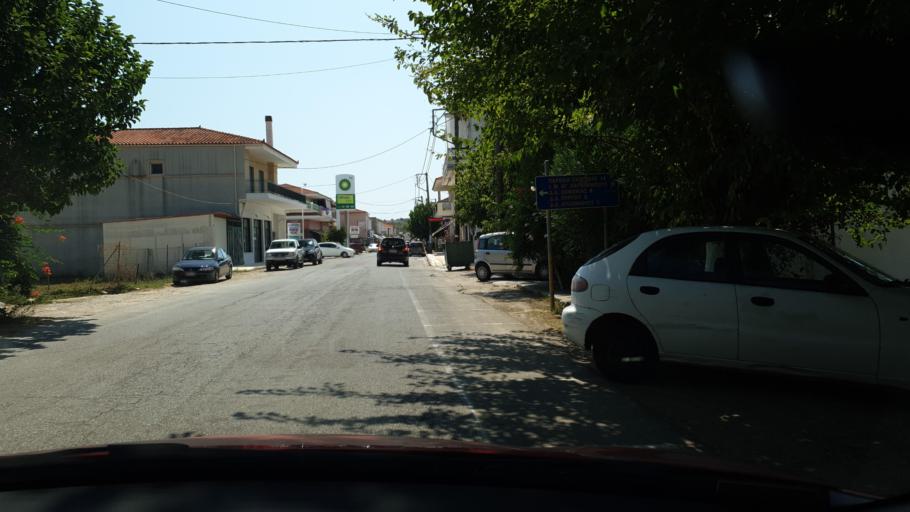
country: GR
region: Central Greece
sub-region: Nomos Evvoias
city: Oxilithos
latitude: 38.5017
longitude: 24.1103
